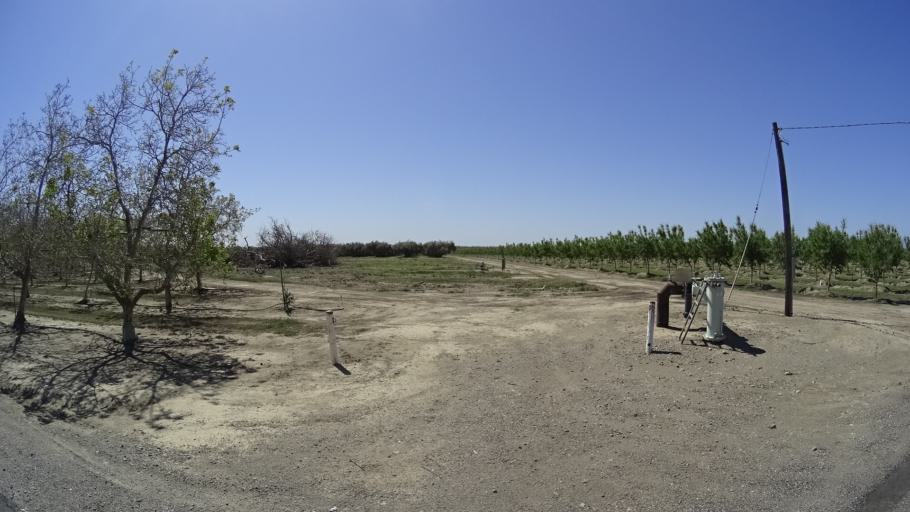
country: US
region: California
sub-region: Glenn County
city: Orland
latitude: 39.7107
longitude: -122.1504
